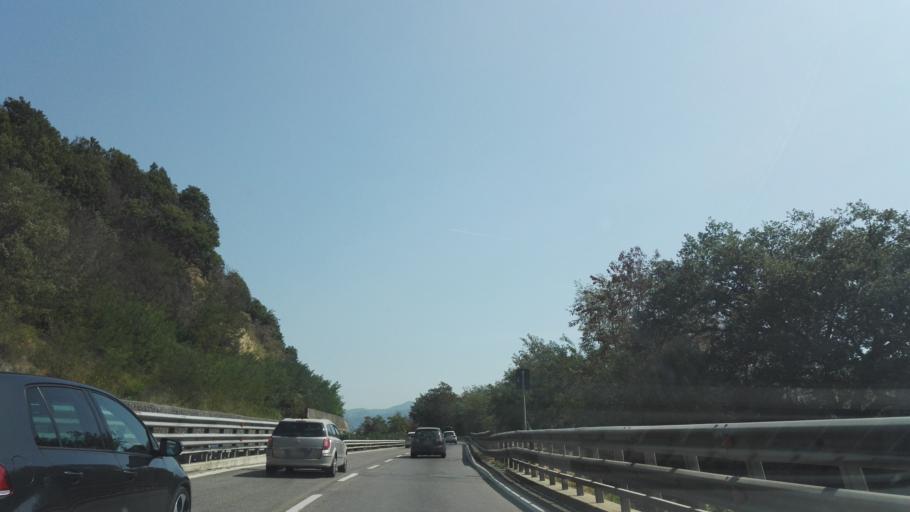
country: IT
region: Calabria
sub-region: Provincia di Cosenza
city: Altilia
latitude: 39.1301
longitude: 16.2671
